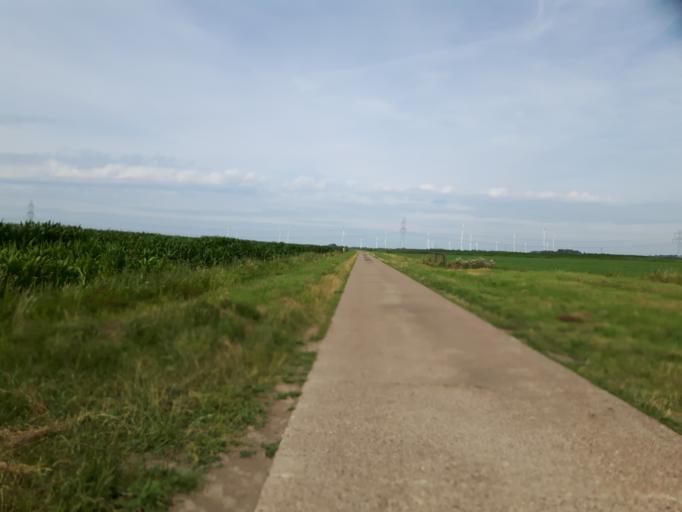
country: DE
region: Lower Saxony
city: Elsfleth
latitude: 53.2595
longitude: 8.4297
